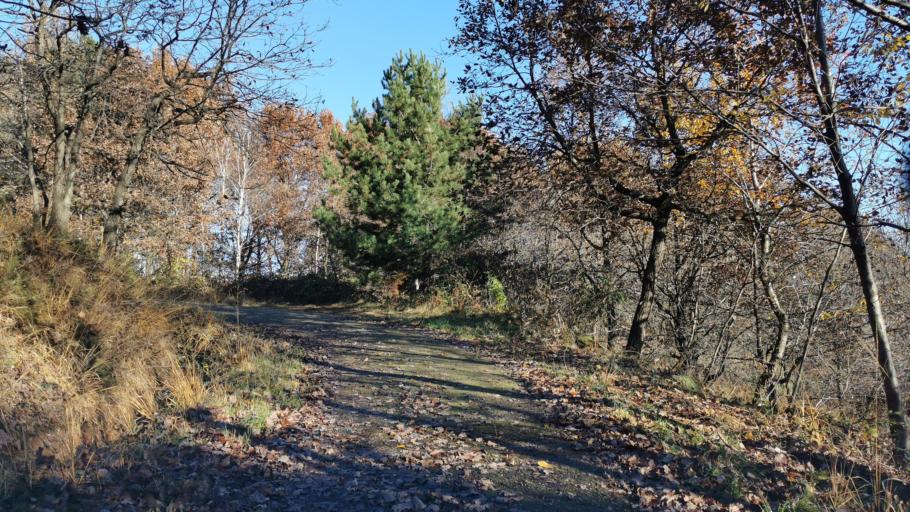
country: IT
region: Piedmont
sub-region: Provincia di Torino
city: La Cassa
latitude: 45.1940
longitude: 7.5055
